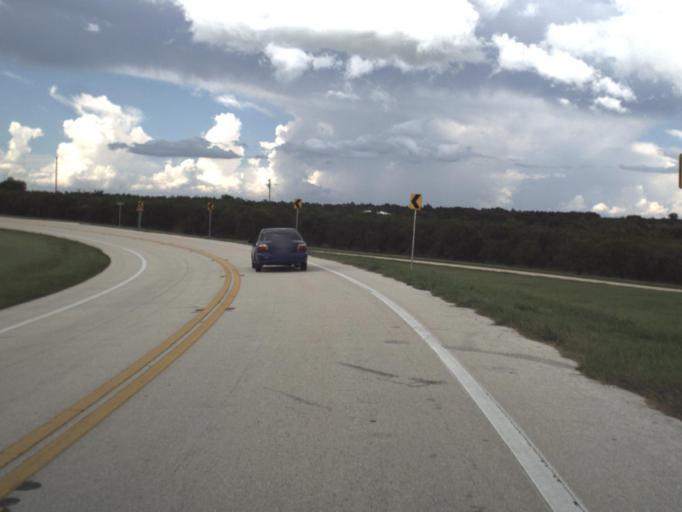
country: US
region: Florida
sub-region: Polk County
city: Fort Meade
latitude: 27.7474
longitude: -81.7282
